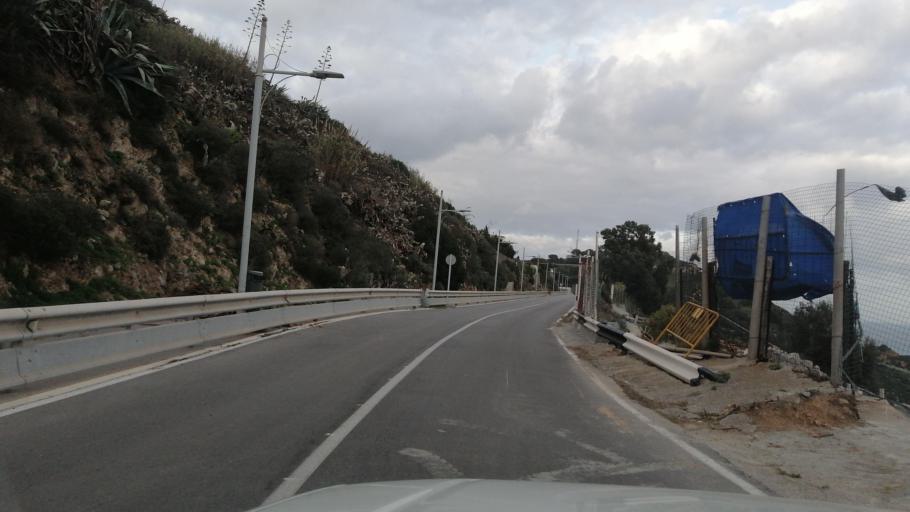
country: ES
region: Ceuta
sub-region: Ceuta
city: Ceuta
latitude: 35.8929
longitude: -5.2870
